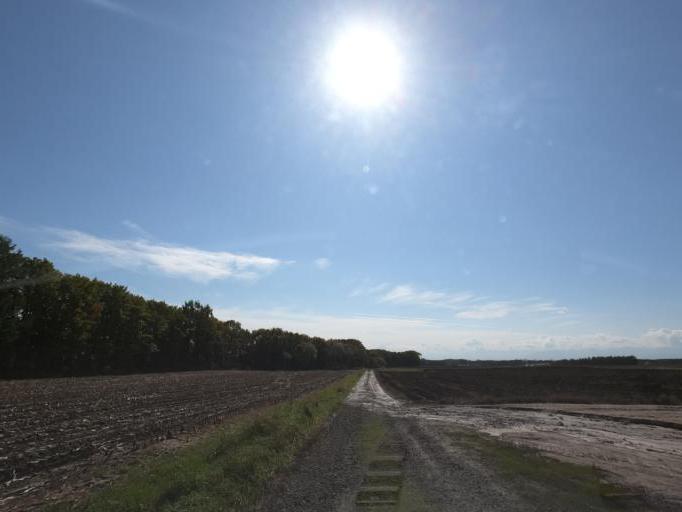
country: JP
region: Hokkaido
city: Otofuke
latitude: 43.2371
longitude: 143.2615
